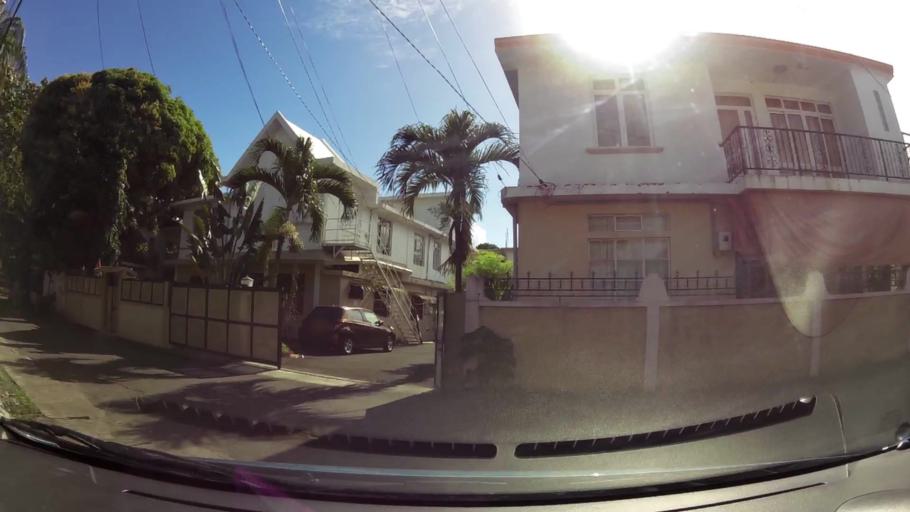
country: MU
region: Grand Port
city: Mahebourg
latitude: -20.4107
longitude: 57.7036
